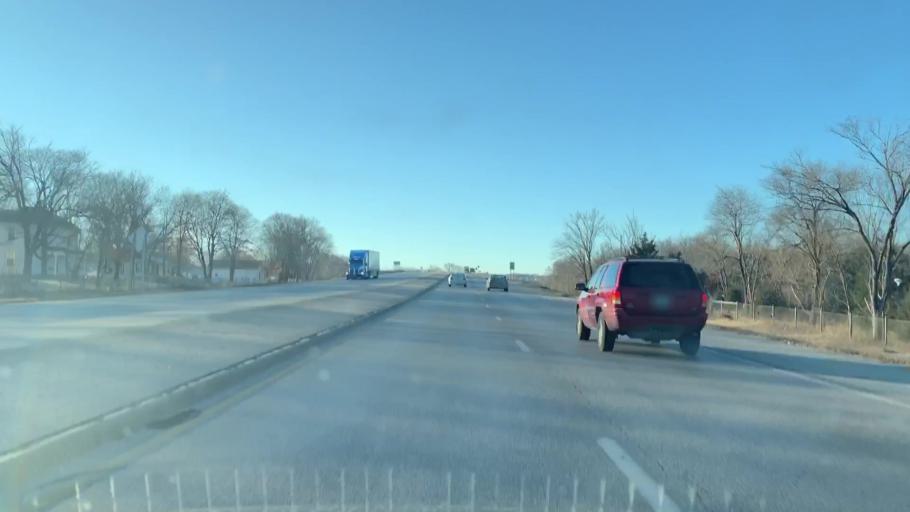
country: US
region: Kansas
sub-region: Bourbon County
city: Fort Scott
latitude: 37.8245
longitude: -94.7043
